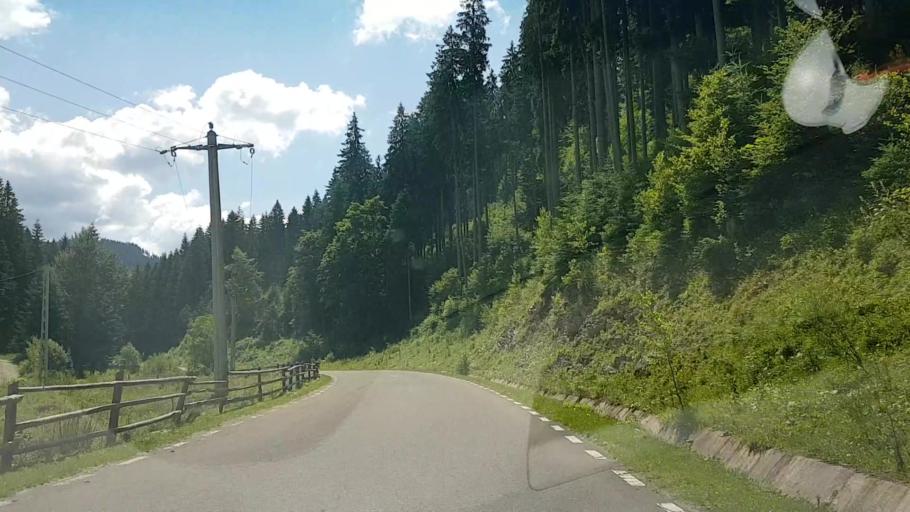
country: RO
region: Suceava
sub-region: Comuna Sadova
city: Sadova
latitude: 47.4800
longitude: 25.4934
